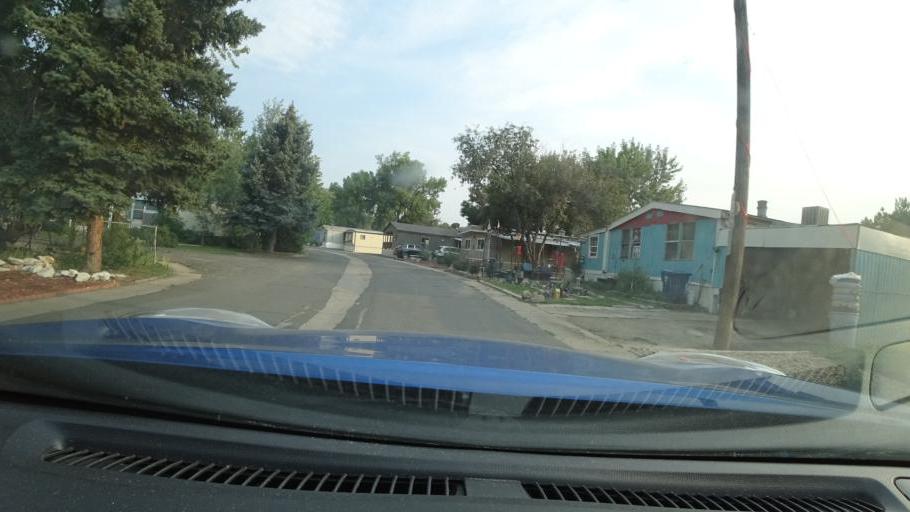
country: US
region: Colorado
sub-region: Adams County
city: Aurora
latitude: 39.7454
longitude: -104.7873
